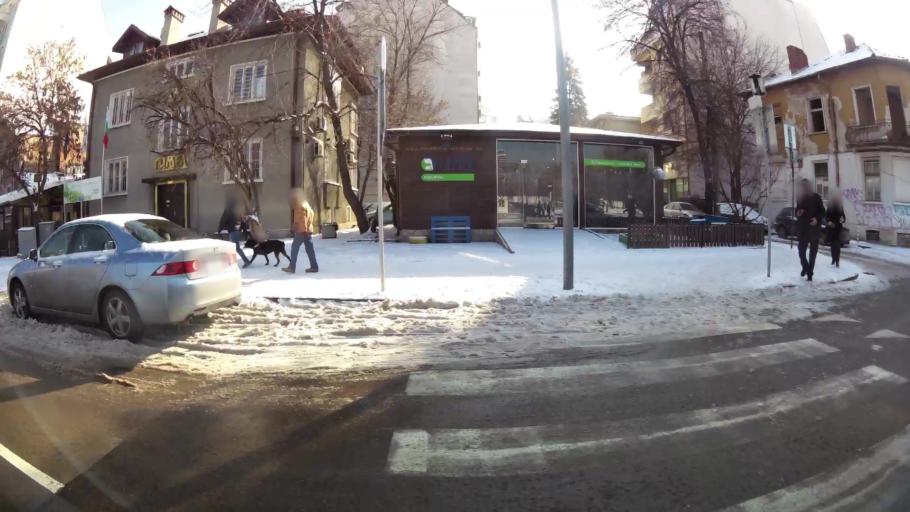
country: BG
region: Sofia-Capital
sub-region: Stolichna Obshtina
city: Sofia
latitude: 42.6776
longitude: 23.3196
